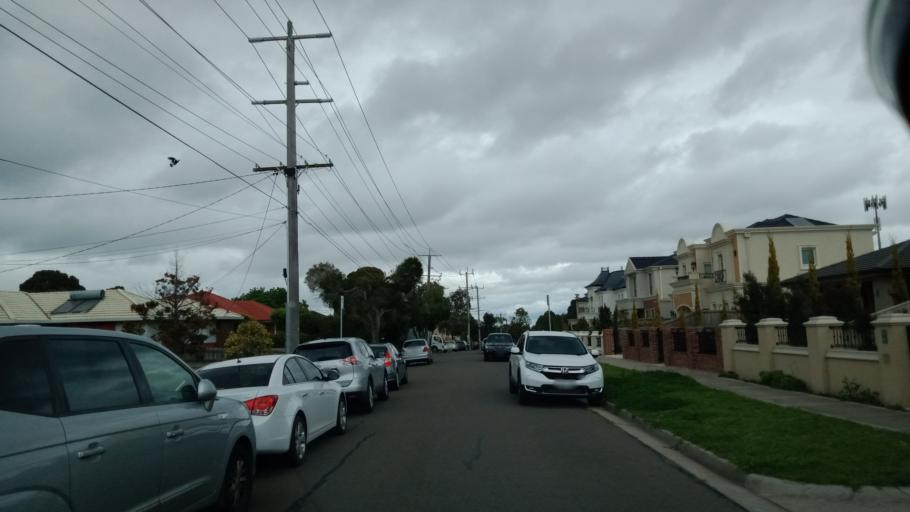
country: AU
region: Victoria
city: Burwood East
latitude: -37.8767
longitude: 145.1575
